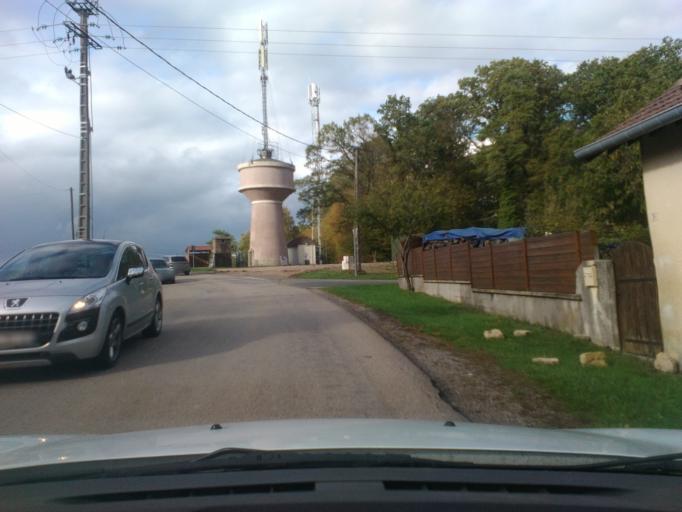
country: FR
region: Lorraine
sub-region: Departement des Vosges
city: Aydoilles
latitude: 48.2497
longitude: 6.5973
